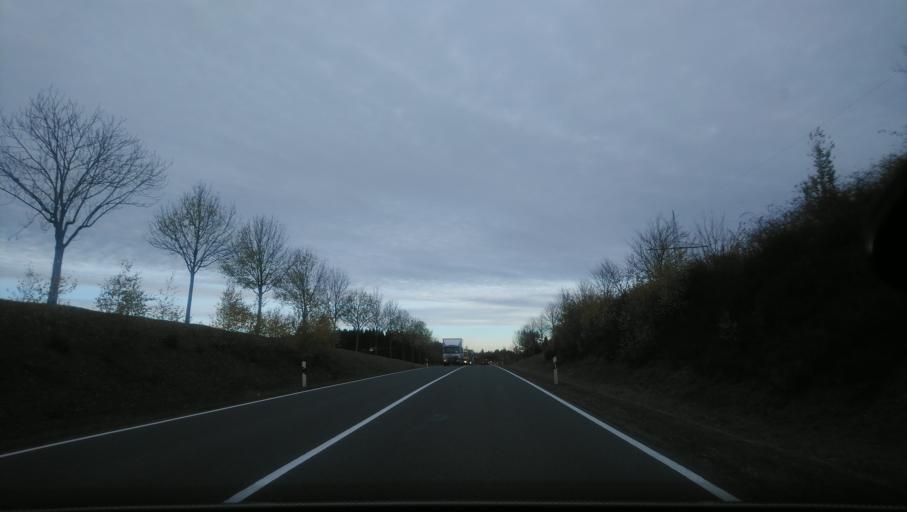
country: DE
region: Saxony
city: Stollberg
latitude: 50.6880
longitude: 12.8005
